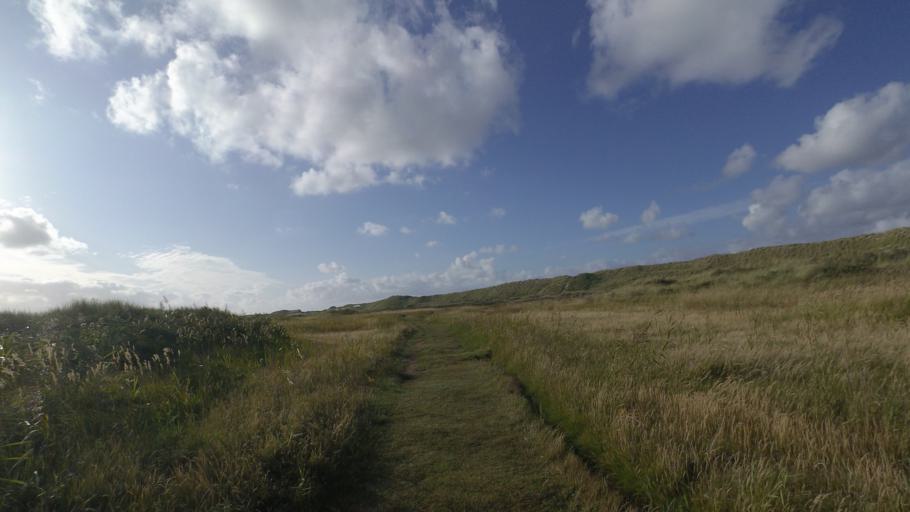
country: NL
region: Friesland
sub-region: Gemeente Dongeradeel
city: Holwerd
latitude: 53.4647
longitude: 5.9130
